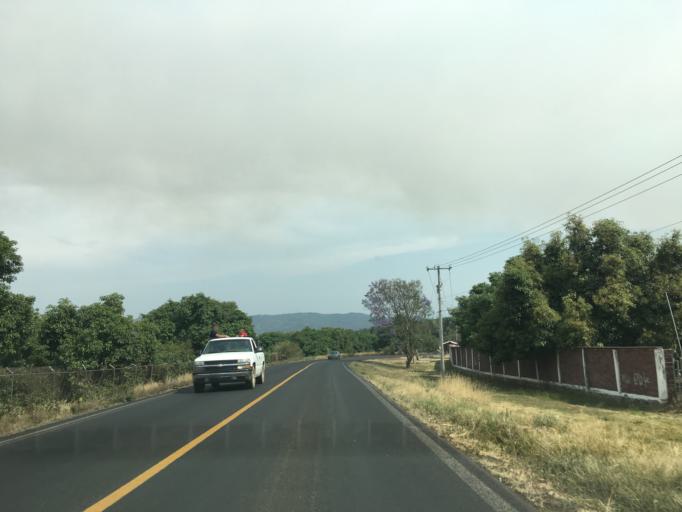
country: MX
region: Michoacan
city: Nuevo San Juan Parangaricutiro
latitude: 19.3983
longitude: -102.1070
